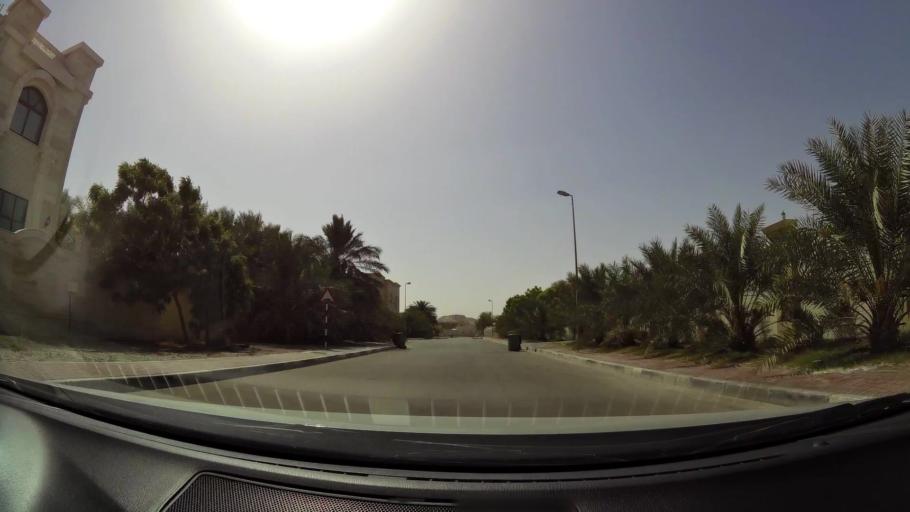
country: OM
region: Al Buraimi
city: Al Buraymi
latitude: 24.3056
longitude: 55.7990
